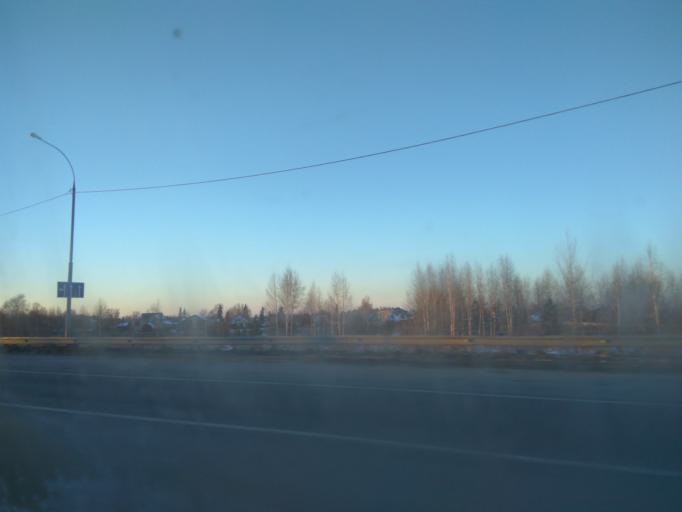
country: RU
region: Novosibirsk
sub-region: Novosibirskiy Rayon
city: Novosibirsk
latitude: 55.1338
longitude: 82.9767
